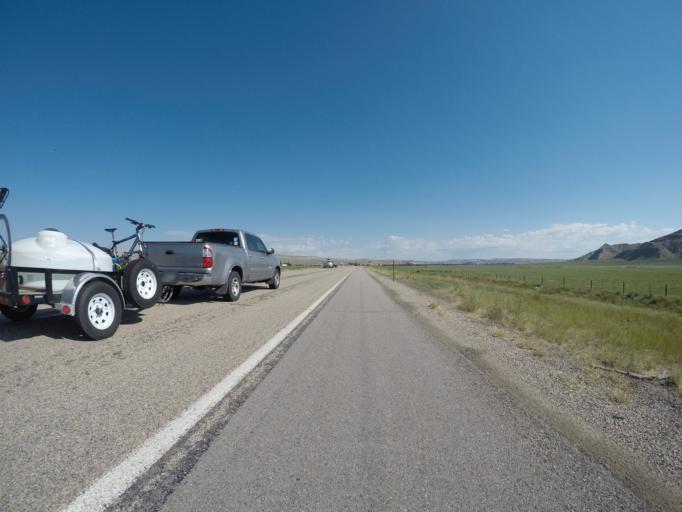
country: US
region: Wyoming
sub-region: Sublette County
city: Marbleton
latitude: 42.1460
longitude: -110.1853
